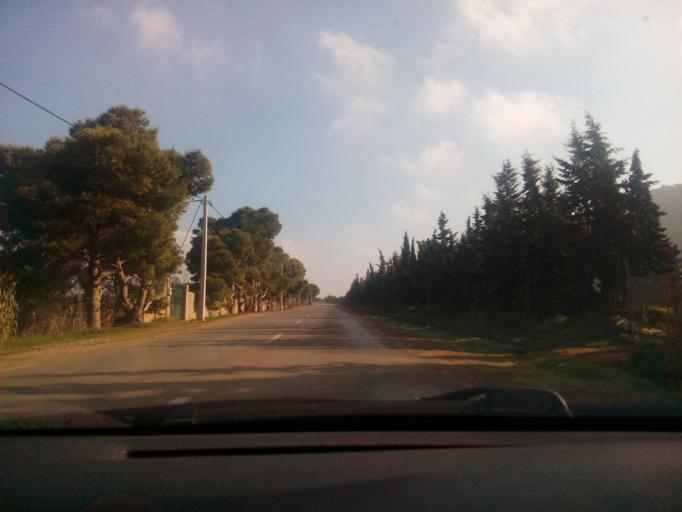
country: DZ
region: Oran
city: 'Ain el Turk
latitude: 35.7038
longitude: -0.8429
